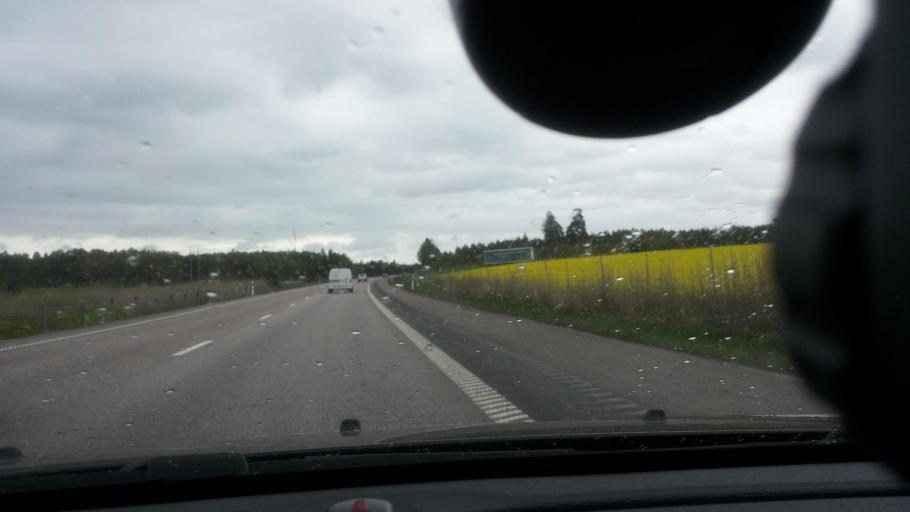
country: SE
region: Stockholm
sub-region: Sigtuna Kommun
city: Marsta
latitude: 59.6768
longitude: 17.8704
